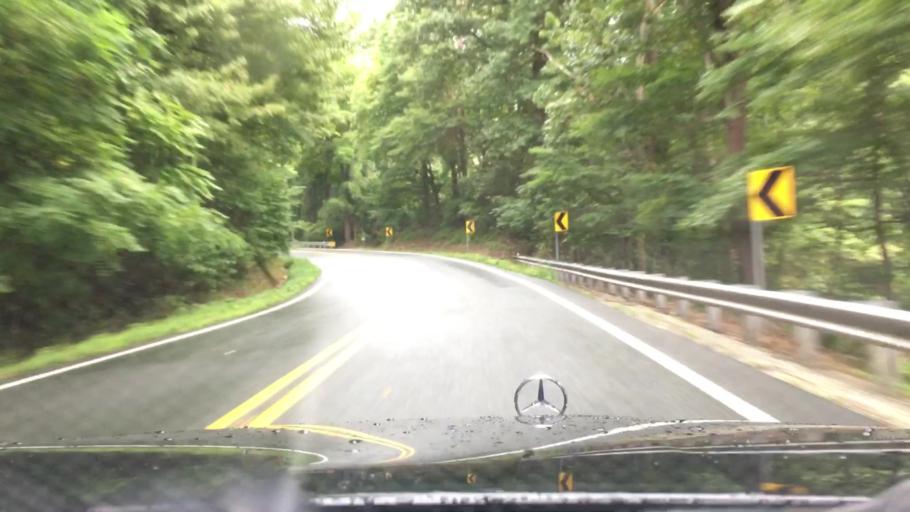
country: US
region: Virginia
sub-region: Nelson County
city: Nellysford
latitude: 37.8629
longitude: -78.9210
